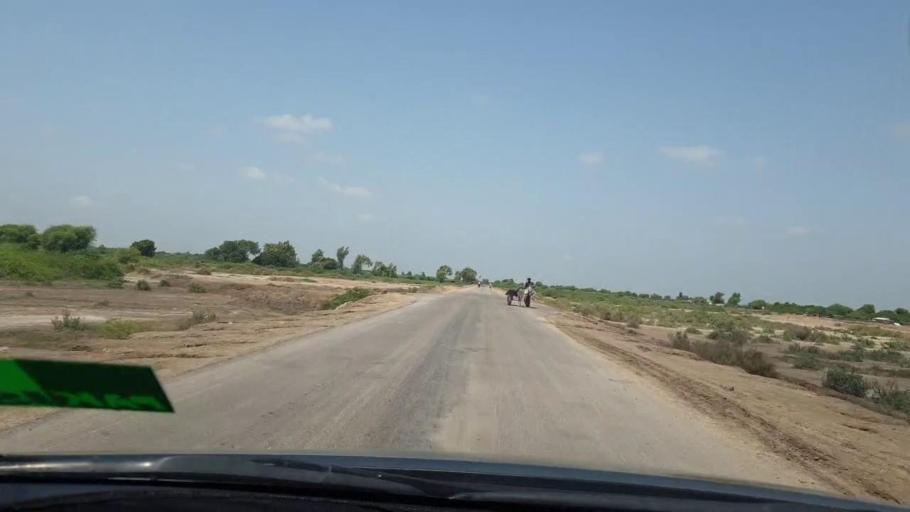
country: PK
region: Sindh
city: Digri
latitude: 24.9919
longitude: 69.1256
